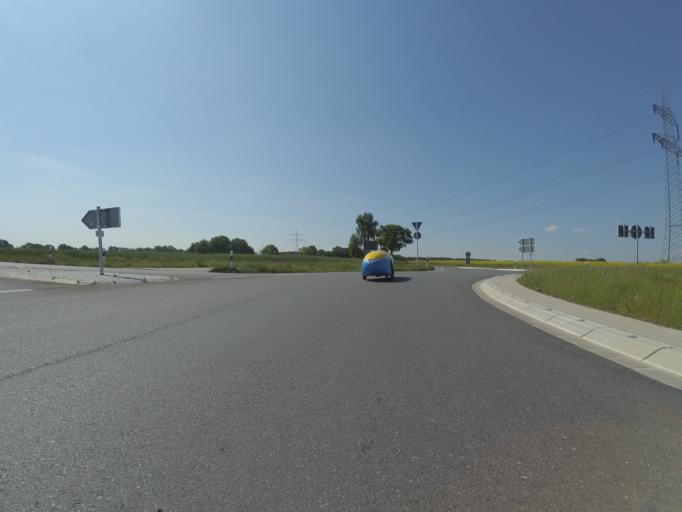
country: DE
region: Lower Saxony
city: Isernhagen Farster Bauerschaft
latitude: 52.4799
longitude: 9.8978
